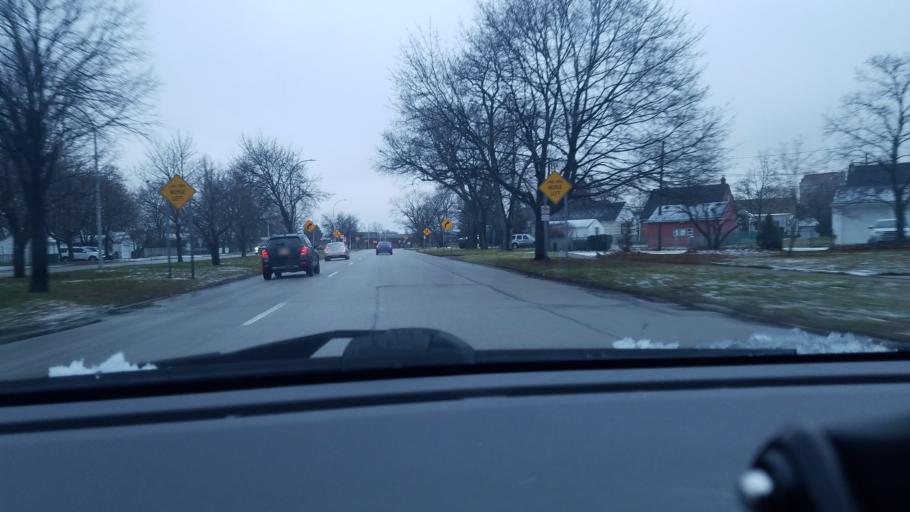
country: US
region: Michigan
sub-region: Wayne County
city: Dearborn Heights
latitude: 42.2971
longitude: -83.2602
